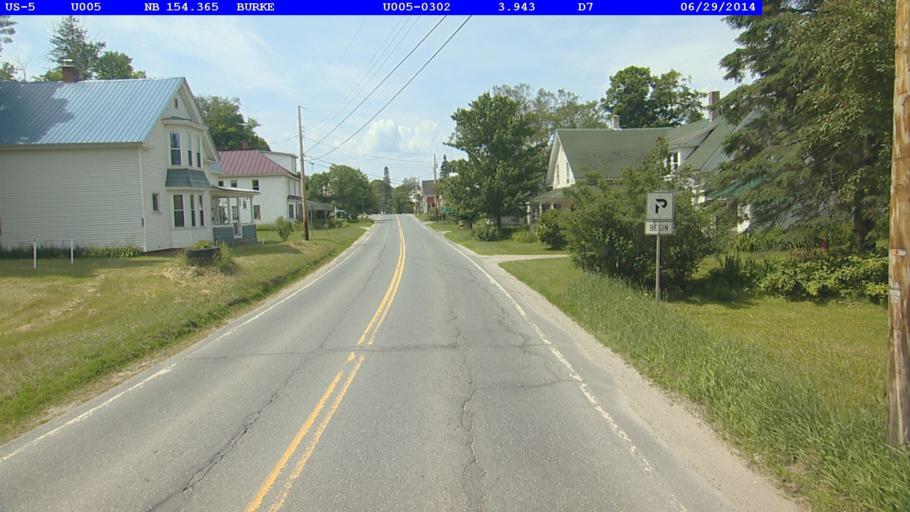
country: US
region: Vermont
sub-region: Caledonia County
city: Lyndonville
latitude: 44.6399
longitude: -71.9783
